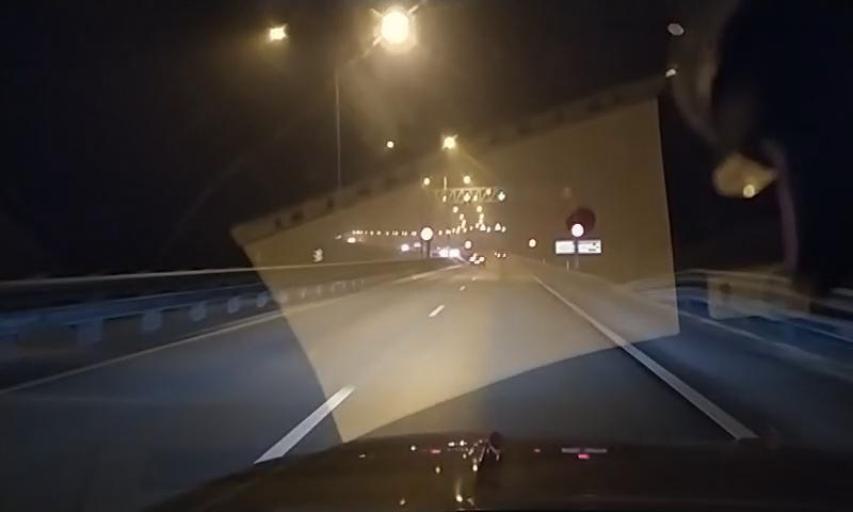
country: RU
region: Leningrad
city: Bugry
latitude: 60.1056
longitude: 30.3864
